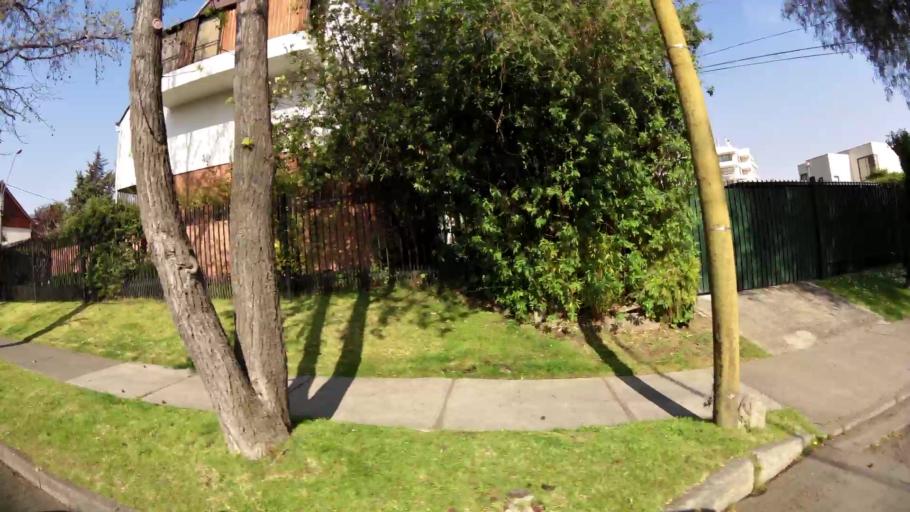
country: CL
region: Santiago Metropolitan
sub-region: Provincia de Santiago
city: Villa Presidente Frei, Nunoa, Santiago, Chile
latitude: -33.3839
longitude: -70.5611
